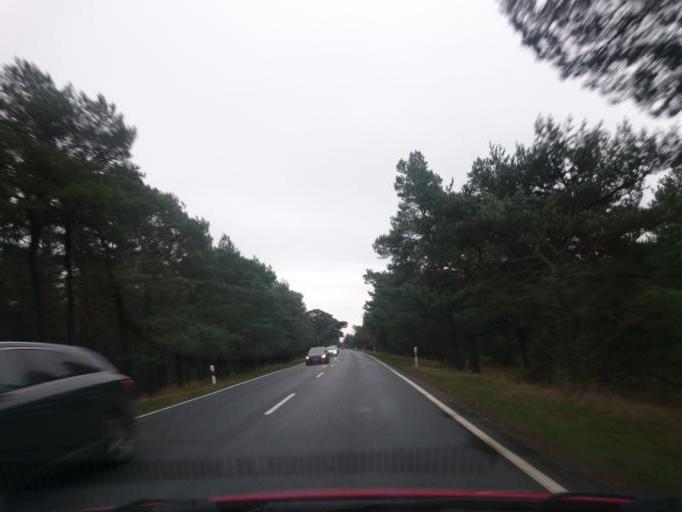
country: DE
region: Mecklenburg-Vorpommern
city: Altenkirchen
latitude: 54.6056
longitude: 13.3830
